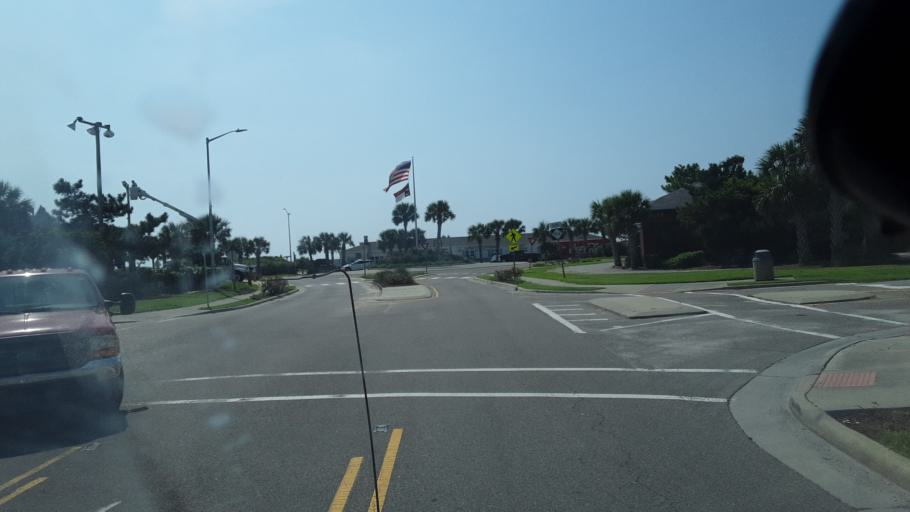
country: US
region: North Carolina
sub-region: Brunswick County
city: Sunset Beach
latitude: 33.8885
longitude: -78.4369
